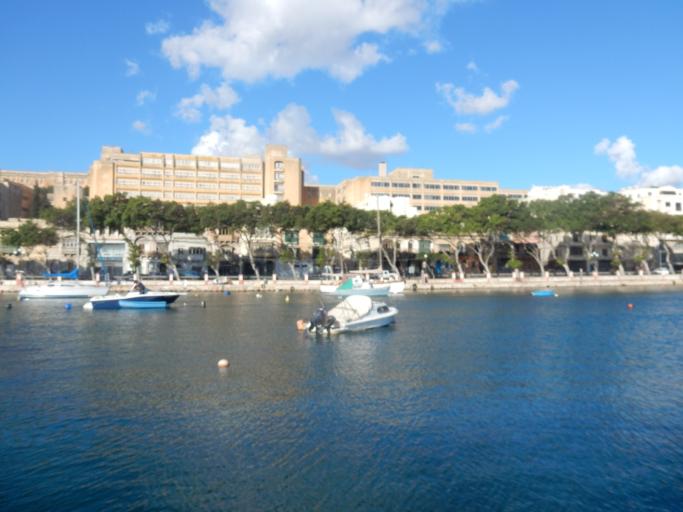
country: MT
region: Tal-Pieta
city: Pieta
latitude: 35.8937
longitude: 14.4980
